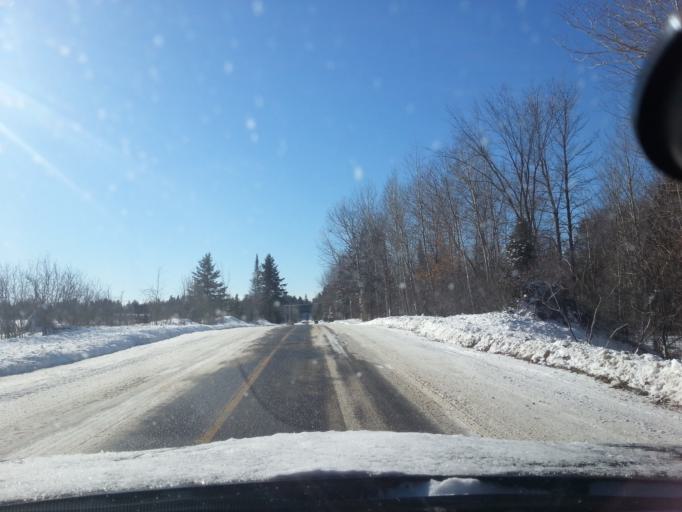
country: CA
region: Ontario
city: Arnprior
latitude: 45.2734
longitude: -76.3127
